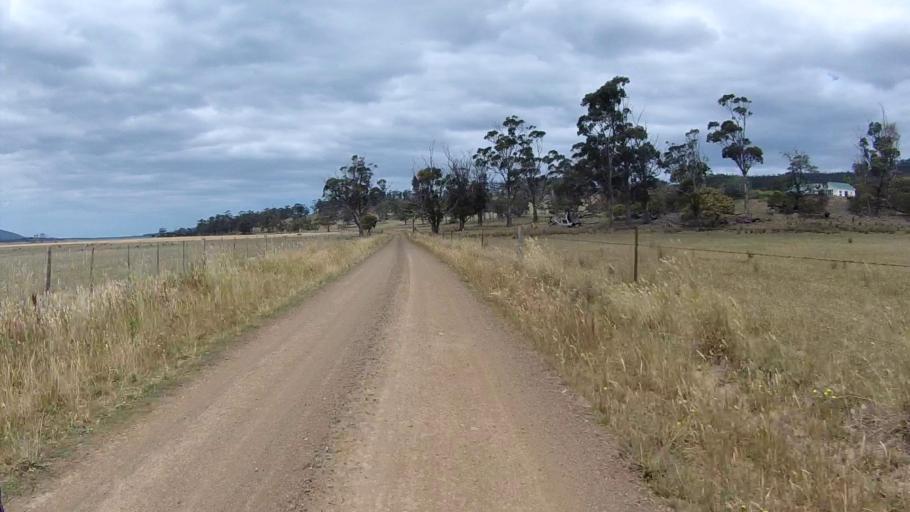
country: AU
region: Tasmania
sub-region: Sorell
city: Sorell
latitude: -42.6590
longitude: 147.9408
